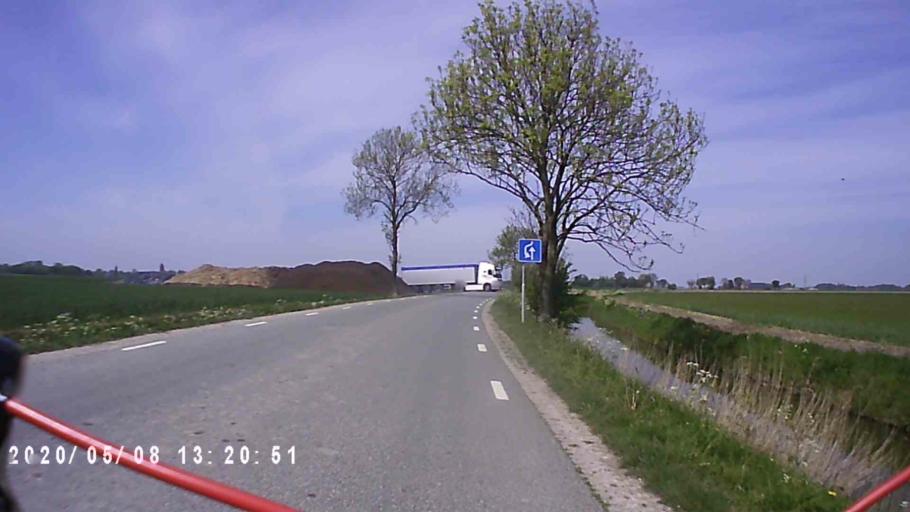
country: NL
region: Groningen
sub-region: Gemeente Bedum
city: Bedum
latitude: 53.3199
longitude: 6.7170
